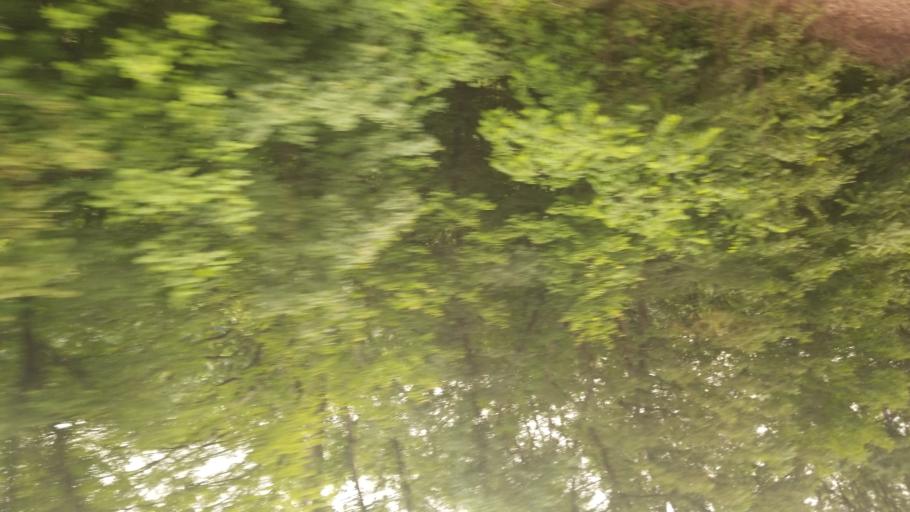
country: US
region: Maryland
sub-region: Allegany County
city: Cumberland
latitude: 39.8285
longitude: -78.7536
